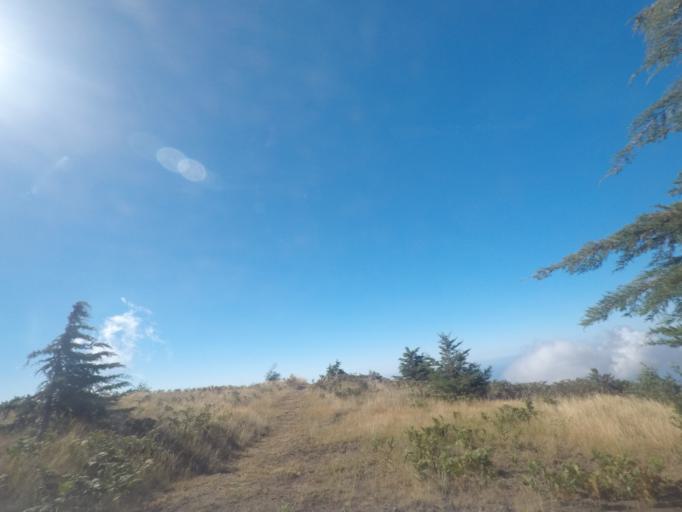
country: PT
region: Madeira
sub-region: Funchal
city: Nossa Senhora do Monte
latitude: 32.7022
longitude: -16.9107
